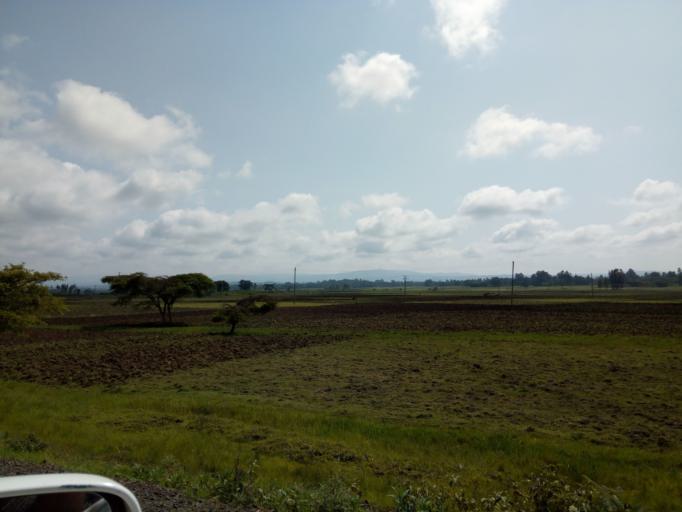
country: ET
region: Oromiya
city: Waliso
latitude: 8.5472
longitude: 37.9579
